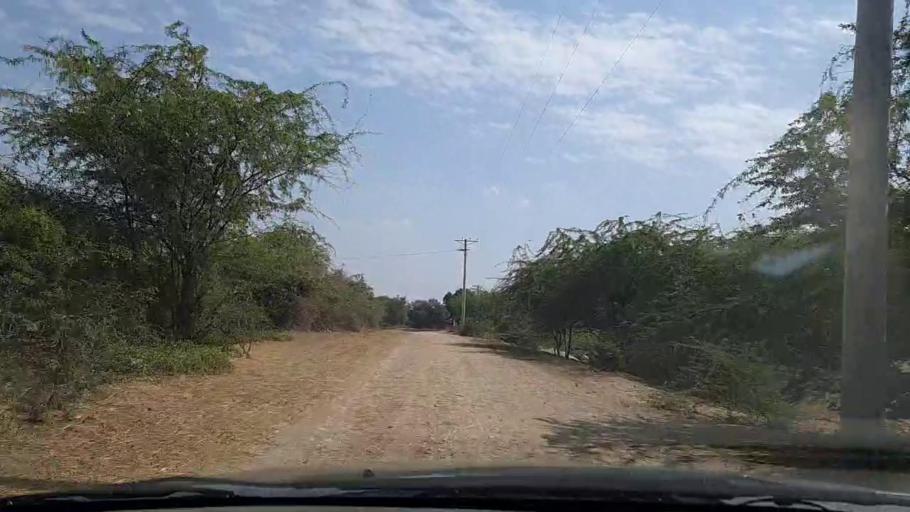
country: PK
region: Sindh
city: Mirpur Batoro
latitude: 24.5630
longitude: 68.2008
